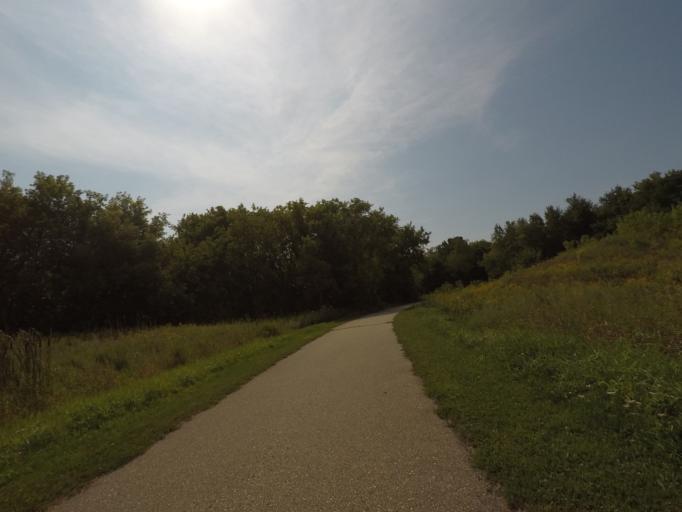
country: US
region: Wisconsin
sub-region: Jefferson County
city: Fort Atkinson
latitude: 42.9554
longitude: -88.8277
